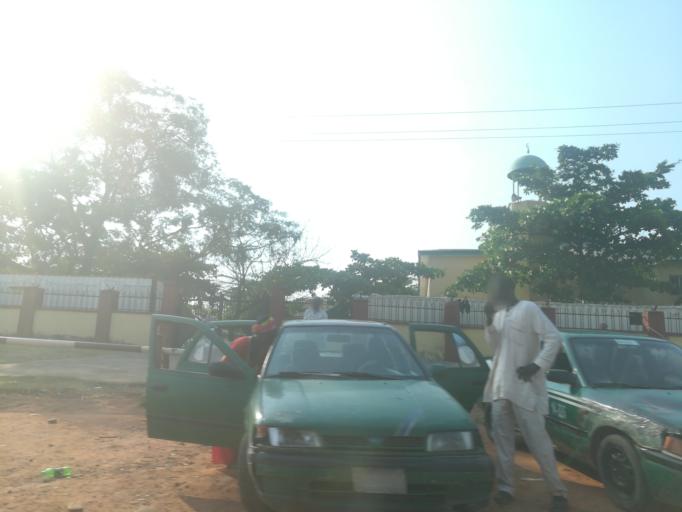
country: NG
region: Abuja Federal Capital Territory
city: Abuja
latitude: 9.0712
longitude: 7.4517
